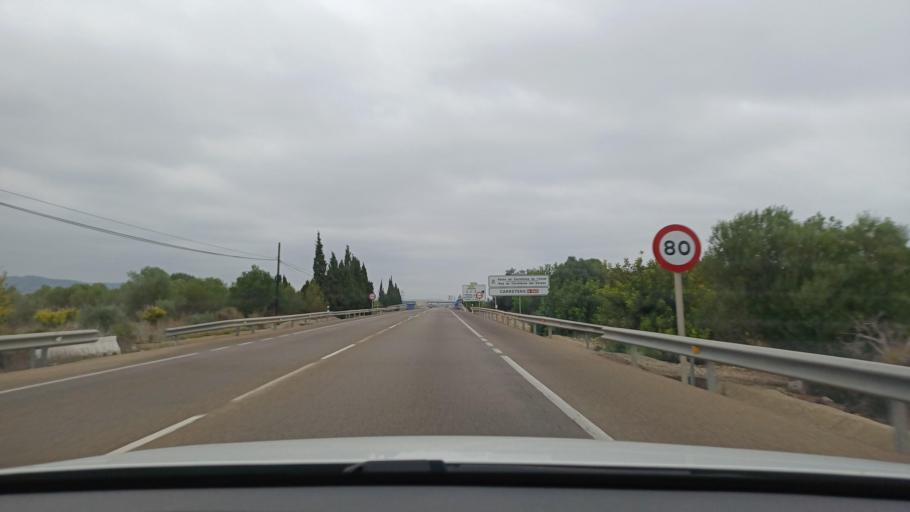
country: ES
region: Valencia
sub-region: Provincia de Castello
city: Orpesa/Oropesa del Mar
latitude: 40.1134
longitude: 0.1398
